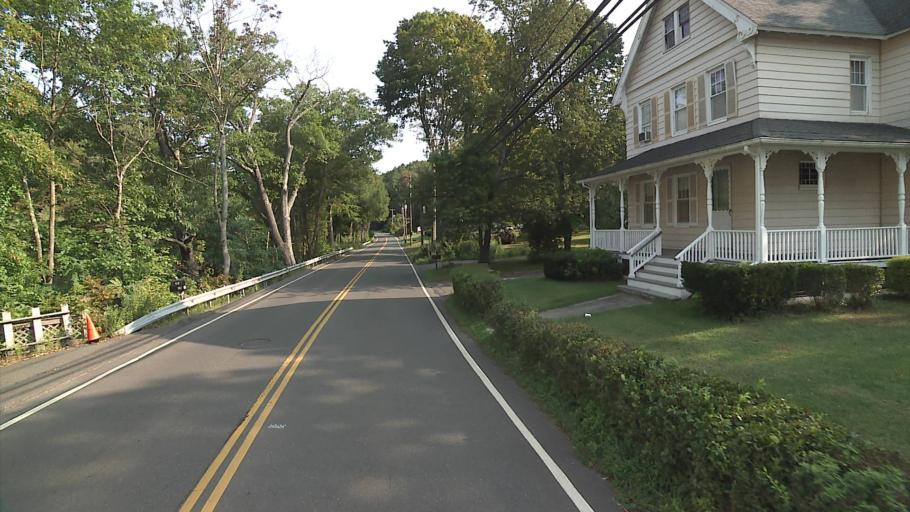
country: US
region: Connecticut
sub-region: Fairfield County
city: Newtown
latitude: 41.4221
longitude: -73.2818
